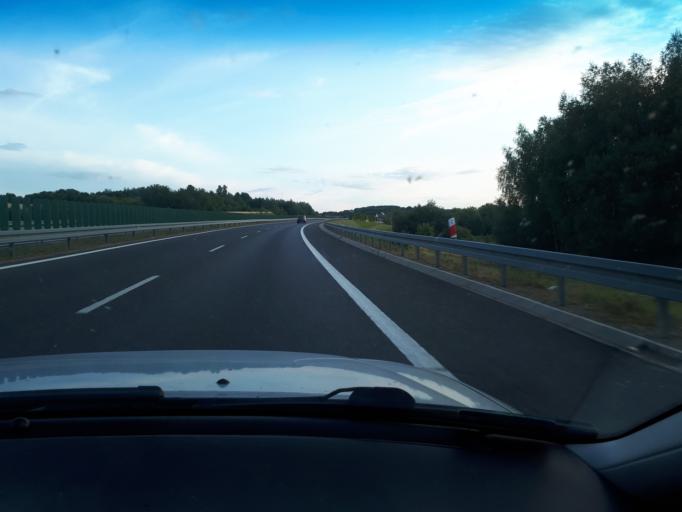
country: PL
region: Subcarpathian Voivodeship
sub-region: Powiat ropczycko-sedziszowski
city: Ropczyce
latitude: 50.0532
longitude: 21.6275
